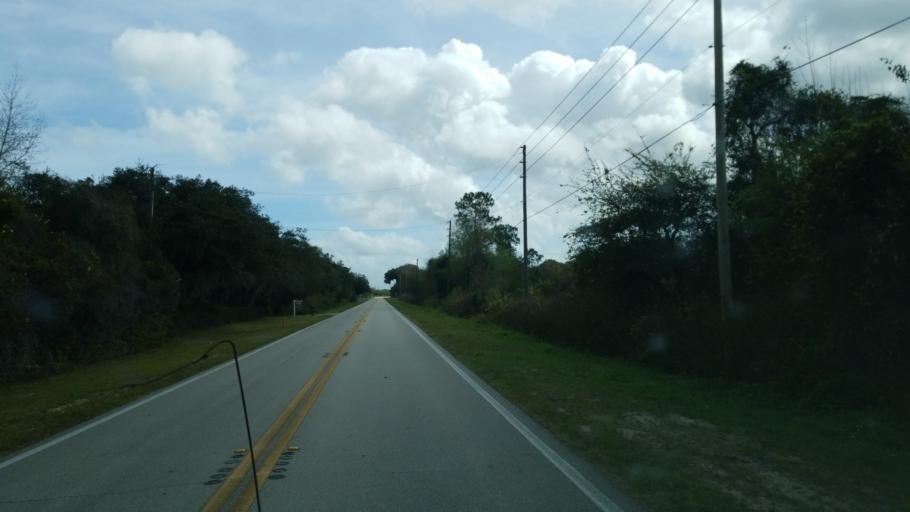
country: US
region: Florida
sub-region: Polk County
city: Haines City
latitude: 28.0774
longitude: -81.5503
